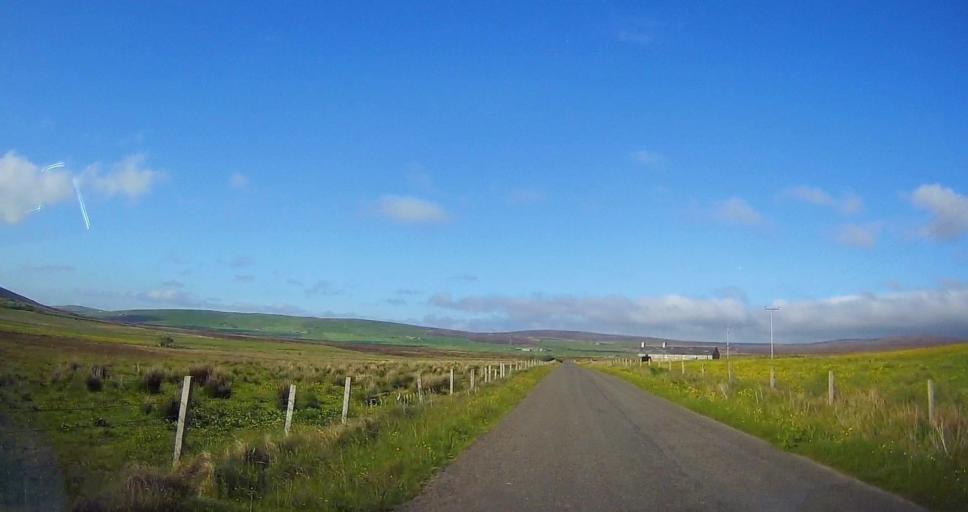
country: GB
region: Scotland
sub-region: Orkney Islands
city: Stromness
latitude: 59.0750
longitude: -3.2055
